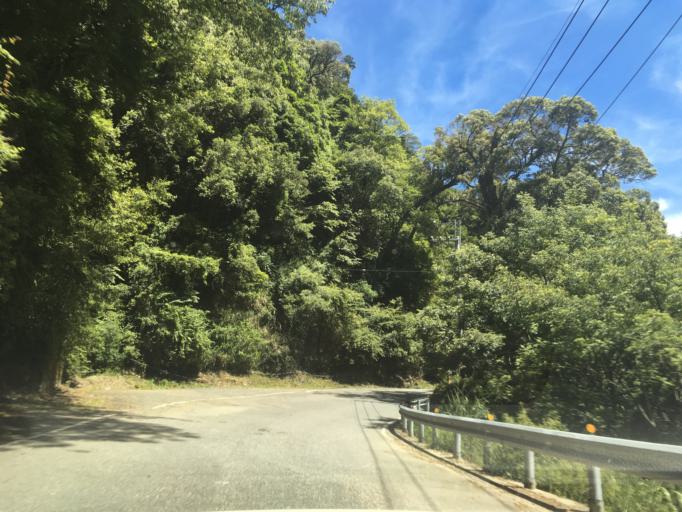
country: TW
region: Taiwan
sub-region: Nantou
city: Puli
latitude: 24.2172
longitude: 121.2648
